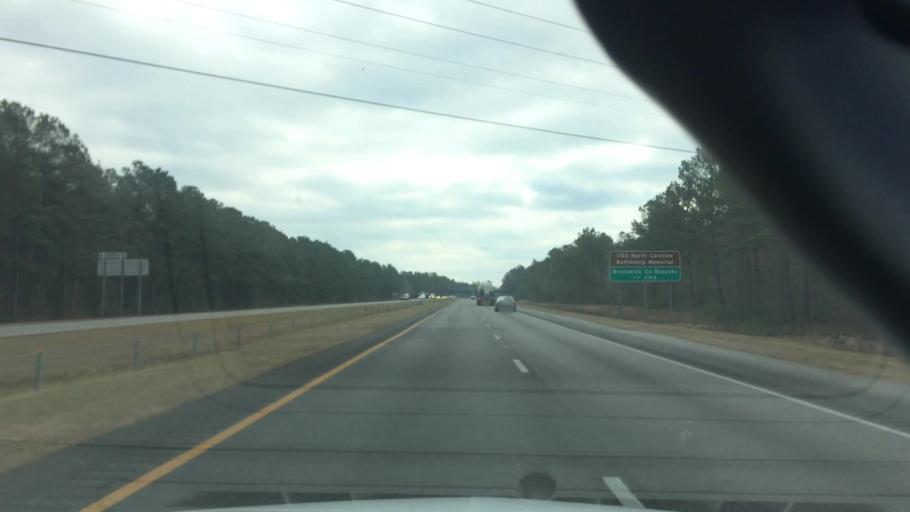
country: US
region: North Carolina
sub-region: New Hanover County
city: Skippers Corner
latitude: 34.3340
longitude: -77.8762
